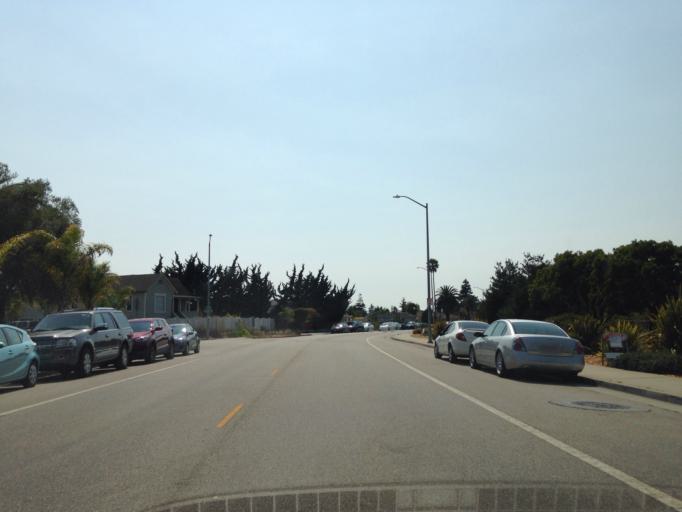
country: US
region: California
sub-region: Santa Cruz County
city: Santa Cruz
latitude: 36.9607
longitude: -122.0287
